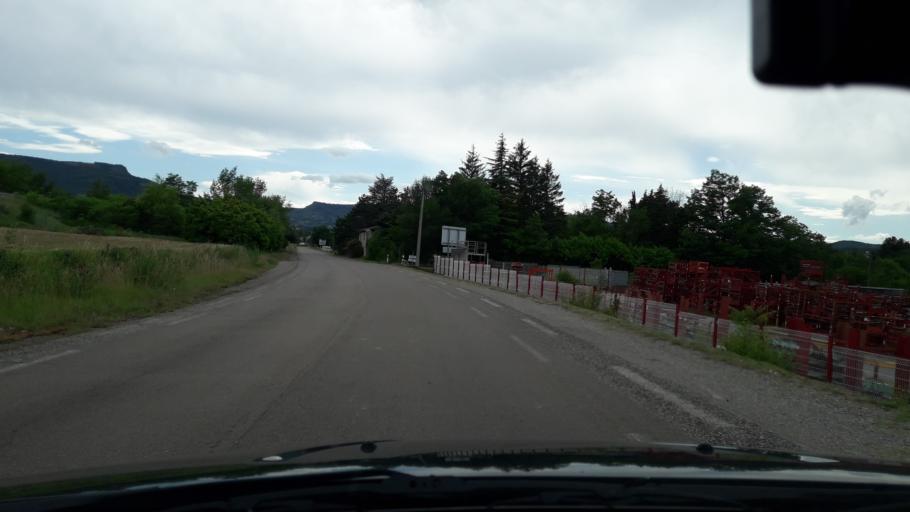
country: FR
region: Rhone-Alpes
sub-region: Departement de l'Ardeche
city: Chomerac
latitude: 44.7121
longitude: 4.7015
